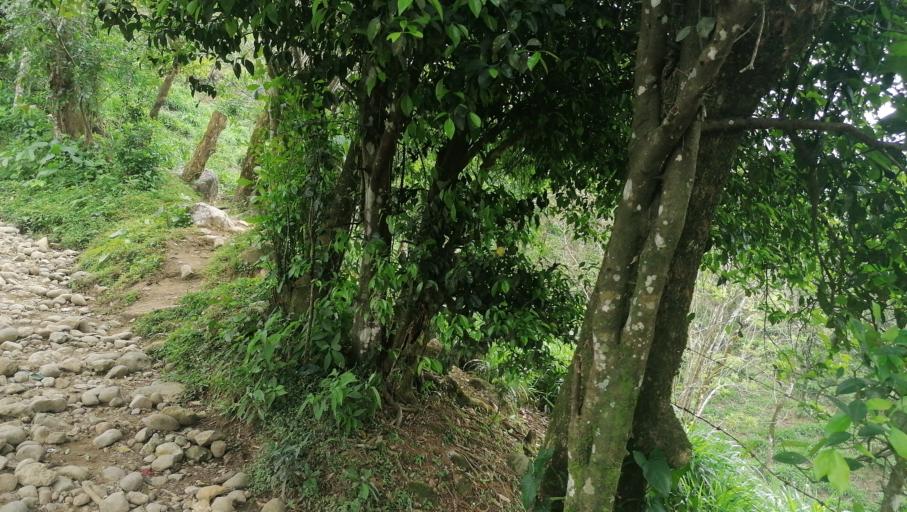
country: MX
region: Chiapas
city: Ocotepec
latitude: 17.2907
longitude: -93.2234
